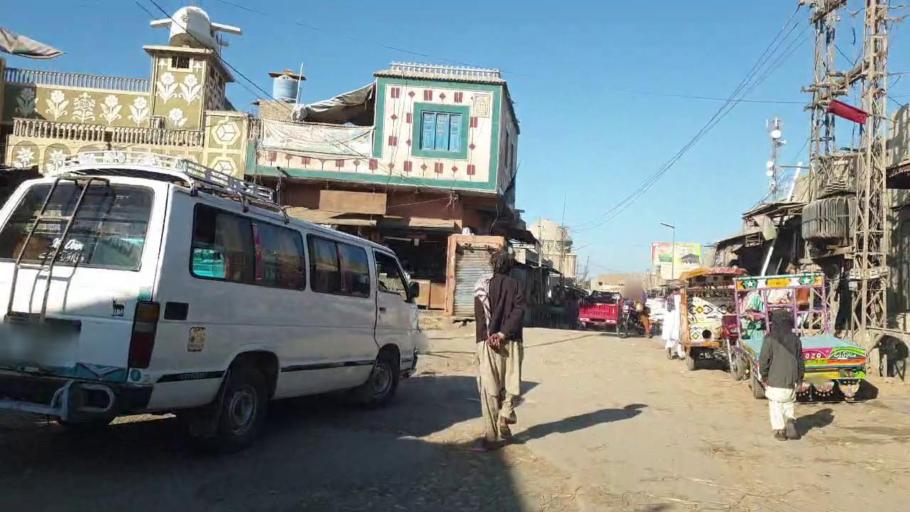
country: PK
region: Sindh
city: New Badah
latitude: 27.3326
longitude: 68.0190
